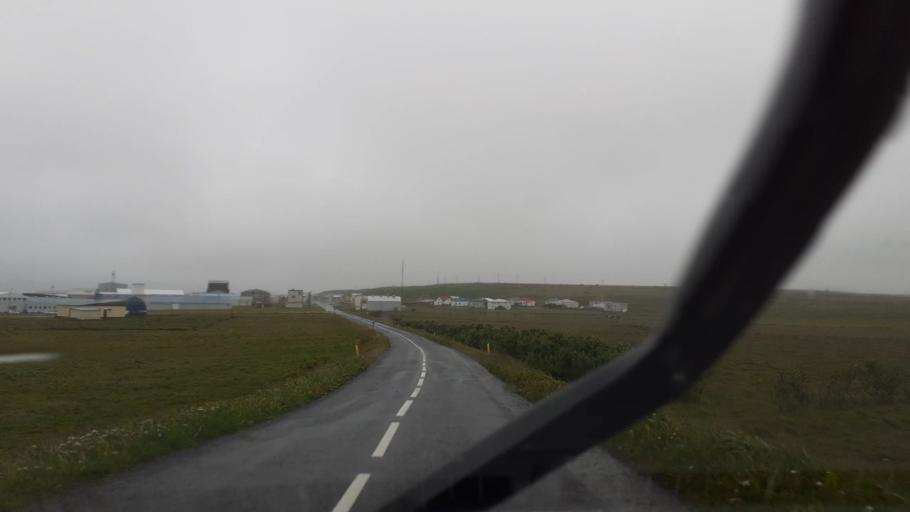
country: IS
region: Northeast
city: Husavik
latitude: 66.4600
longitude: -15.9518
